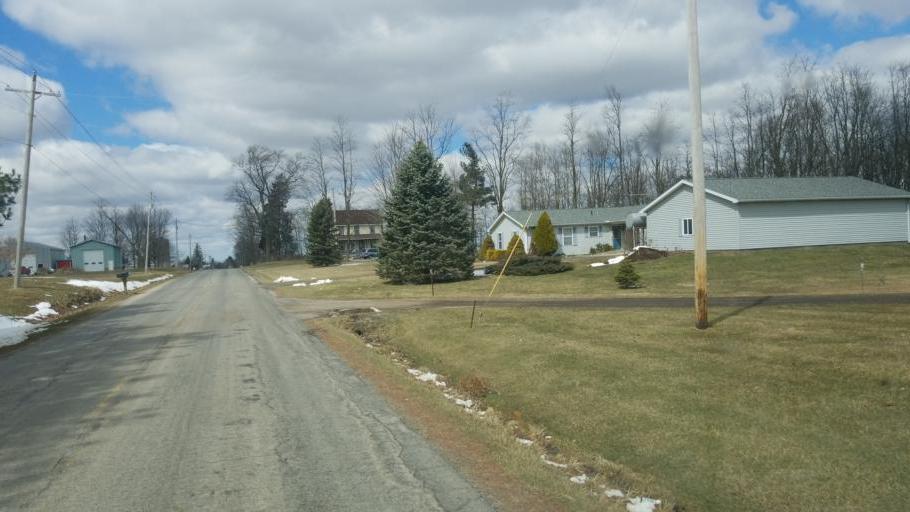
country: US
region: Ohio
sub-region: Richland County
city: Lincoln Heights
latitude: 40.8538
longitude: -82.5193
